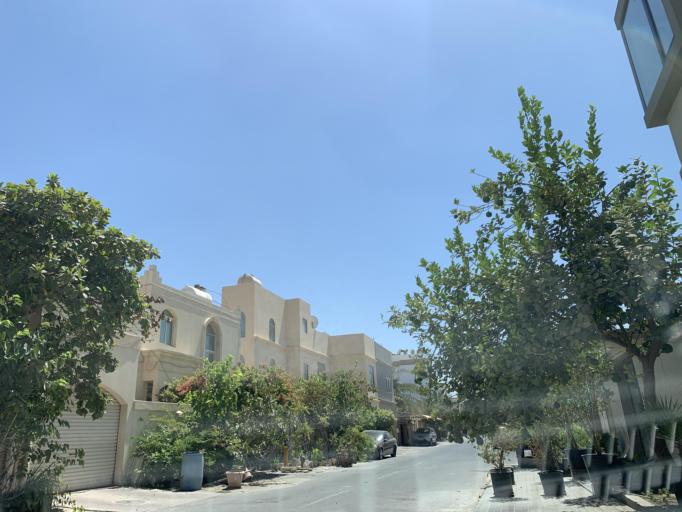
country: BH
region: Manama
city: Jidd Hafs
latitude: 26.2320
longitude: 50.4878
